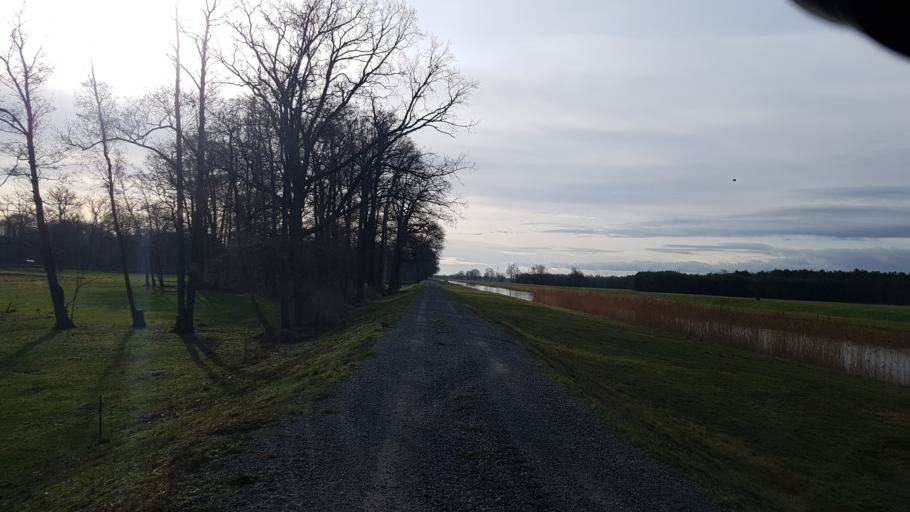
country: DE
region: Brandenburg
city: Falkenberg
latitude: 51.6345
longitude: 13.2786
